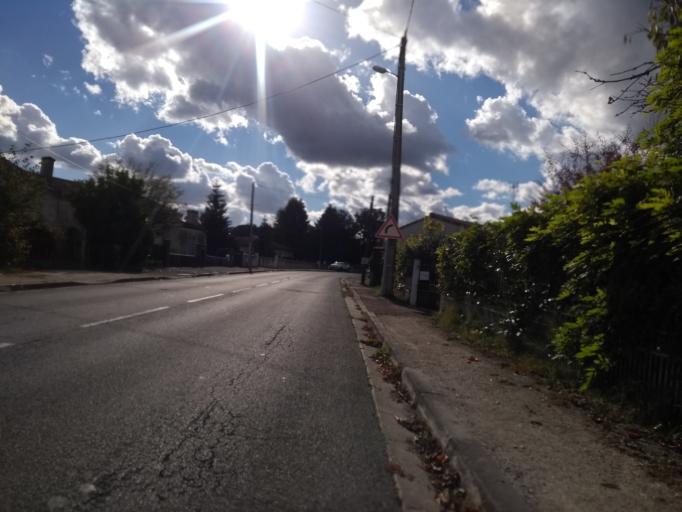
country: FR
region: Aquitaine
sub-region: Departement de la Gironde
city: Canejan
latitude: 44.7640
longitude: -0.6239
